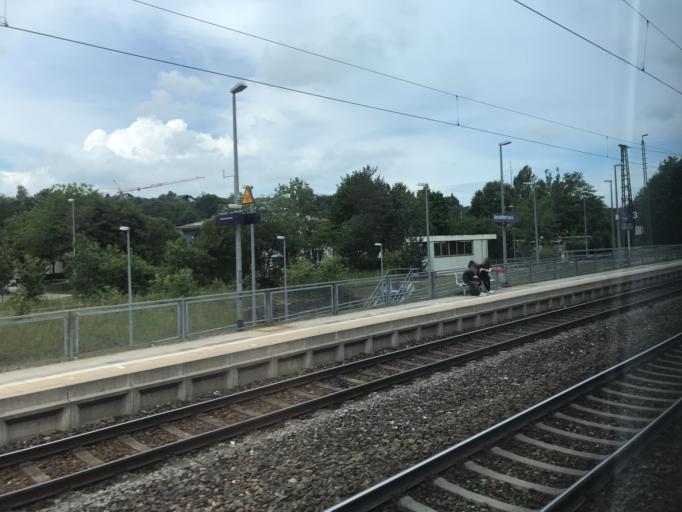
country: DE
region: Baden-Wuerttemberg
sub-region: Tuebingen Region
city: Amstetten
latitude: 48.5777
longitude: 9.8735
